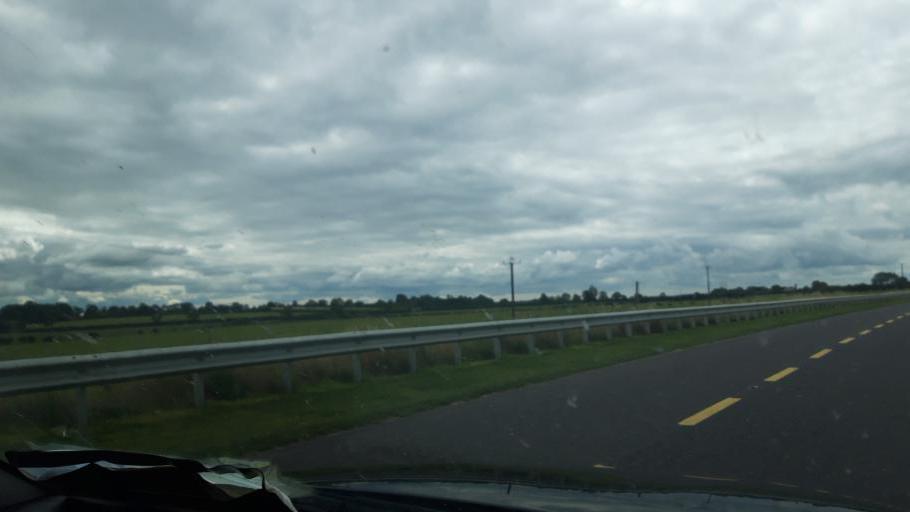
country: IE
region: Leinster
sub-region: Kilkenny
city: Kilkenny
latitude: 52.6203
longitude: -7.2817
